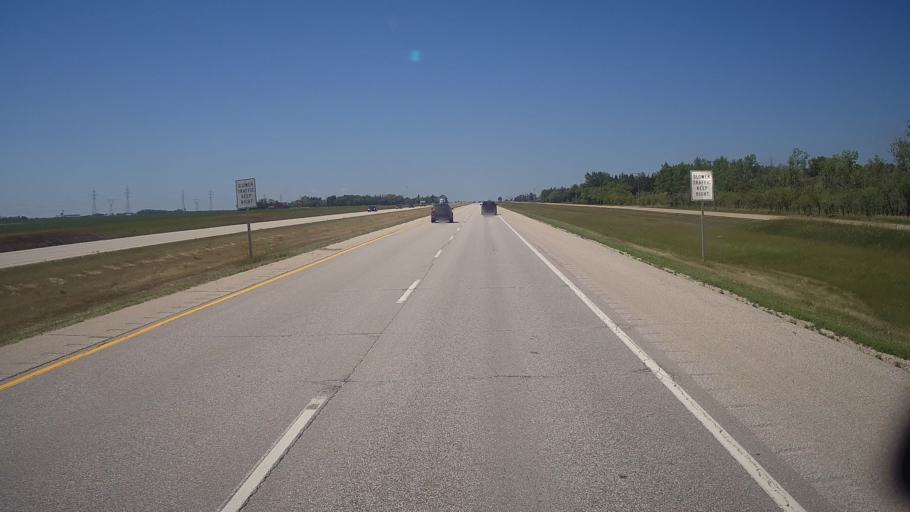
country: CA
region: Manitoba
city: Winnipeg
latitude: 49.9900
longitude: -97.2551
